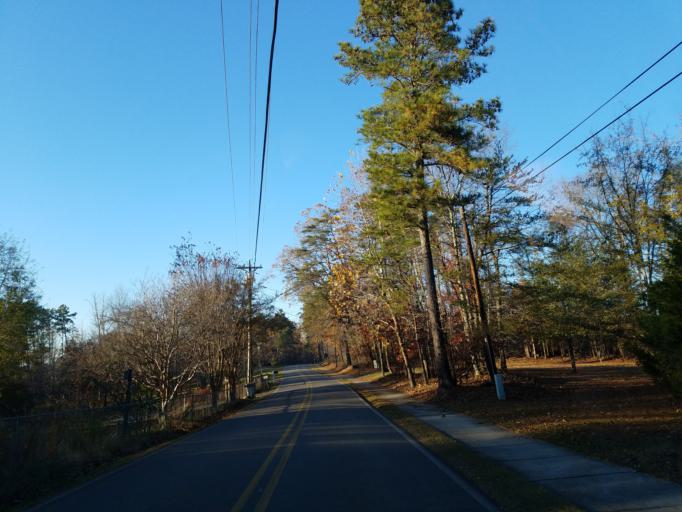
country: US
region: Georgia
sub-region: Pickens County
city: Nelson
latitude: 34.3876
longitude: -84.3694
